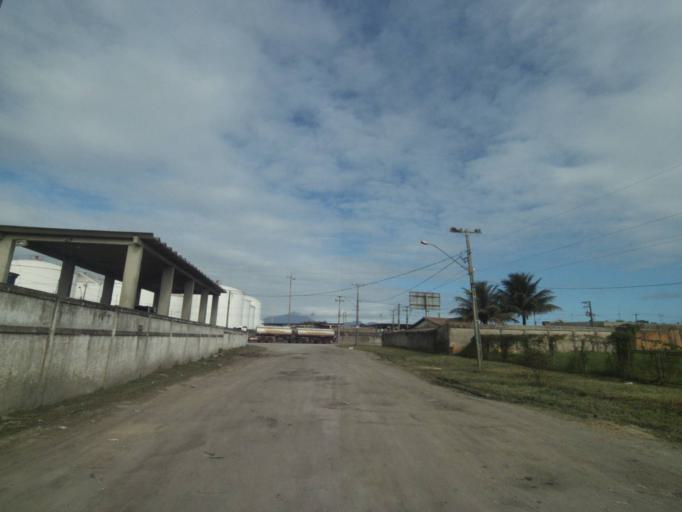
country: BR
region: Parana
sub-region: Paranagua
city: Paranagua
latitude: -25.5087
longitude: -48.5312
